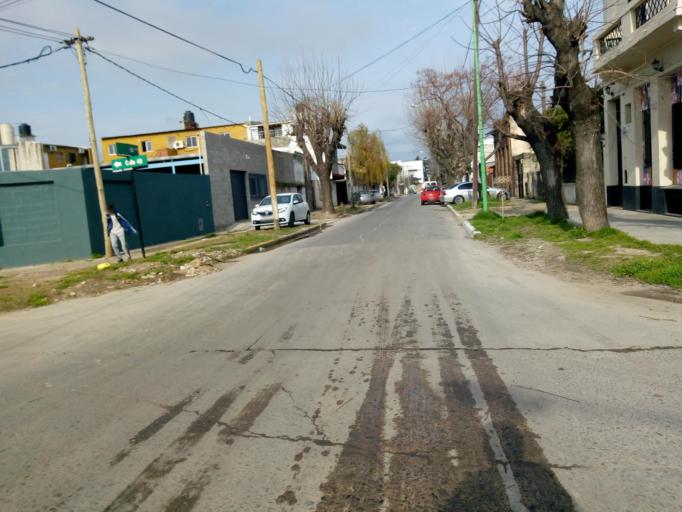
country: AR
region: Buenos Aires
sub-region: Partido de La Plata
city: La Plata
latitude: -34.8991
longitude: -57.9346
